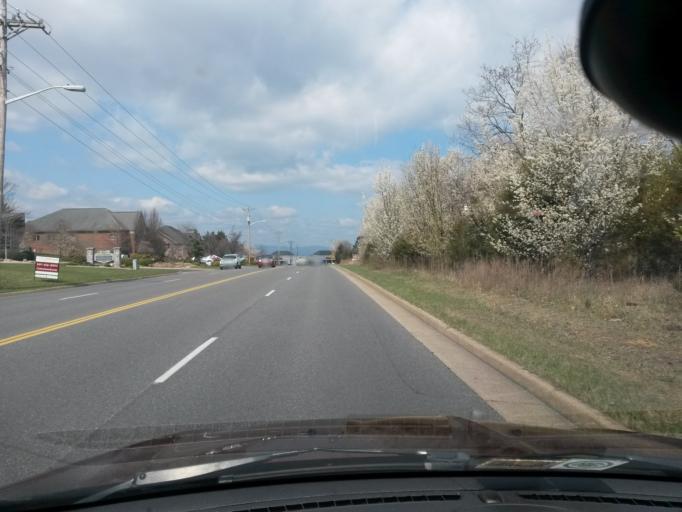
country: US
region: Virginia
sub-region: Rockingham County
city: Massanetta Springs
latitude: 38.4234
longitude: -78.8427
